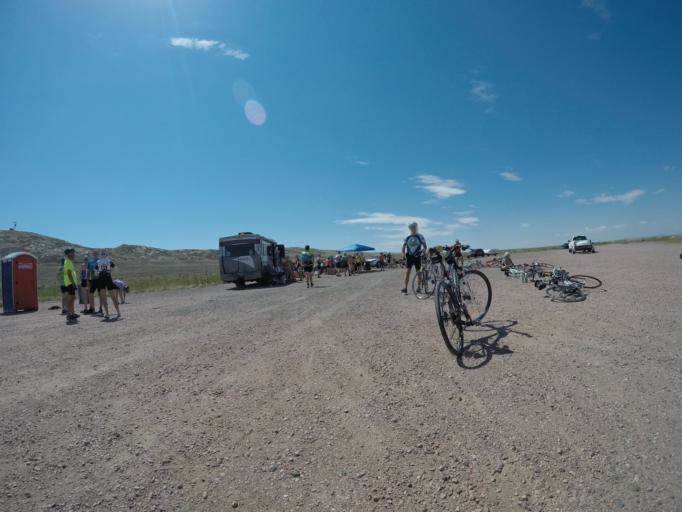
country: US
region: Wyoming
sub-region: Albany County
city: Laramie
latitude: 41.6533
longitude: -105.5352
